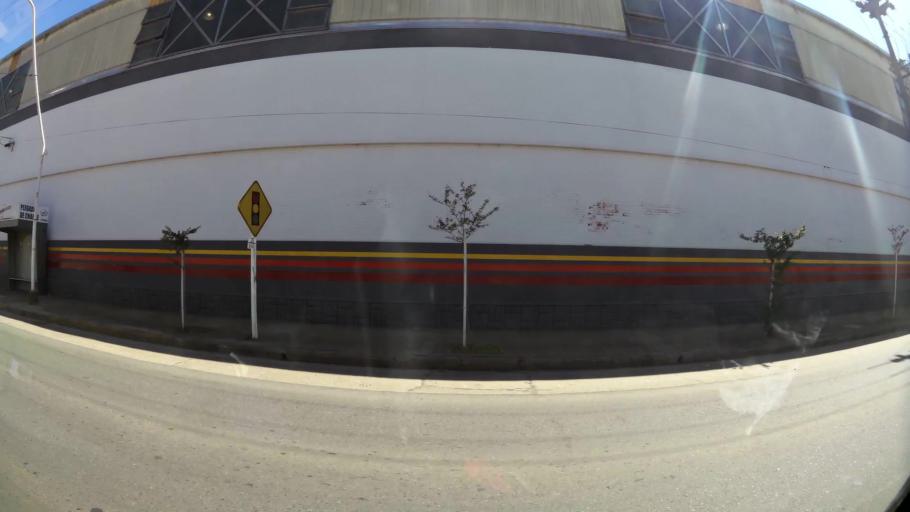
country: AR
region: Santa Fe
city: Esperanza
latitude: -31.4423
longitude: -60.9309
